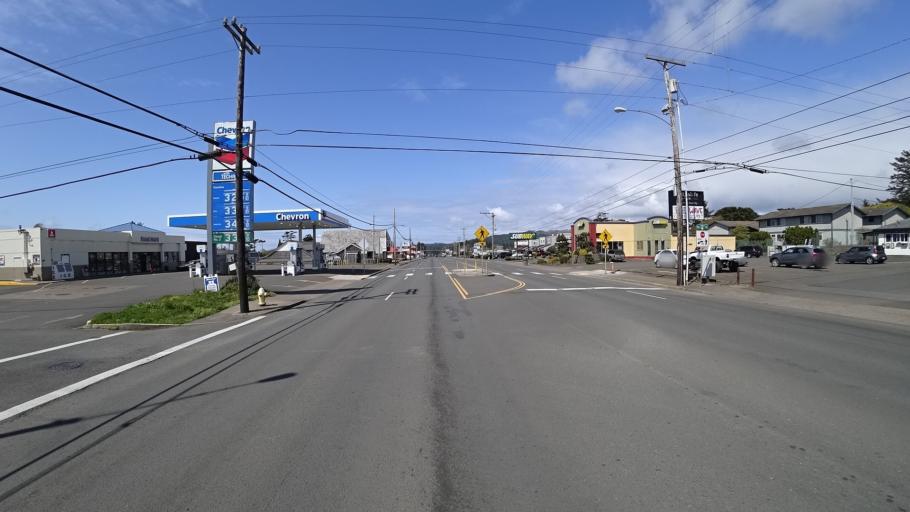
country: US
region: Oregon
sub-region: Lincoln County
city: Newport
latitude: 44.6483
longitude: -124.0531
